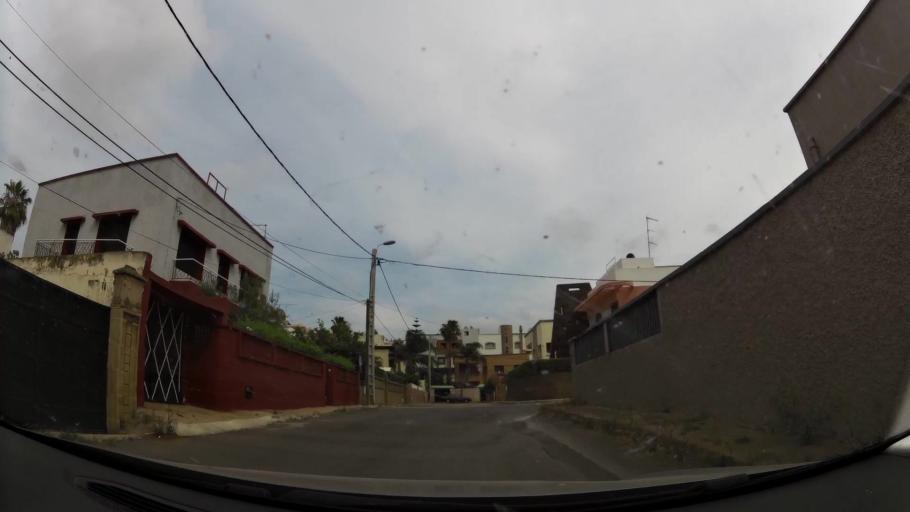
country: MA
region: Rabat-Sale-Zemmour-Zaer
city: Sale
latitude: 34.0282
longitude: -6.8088
